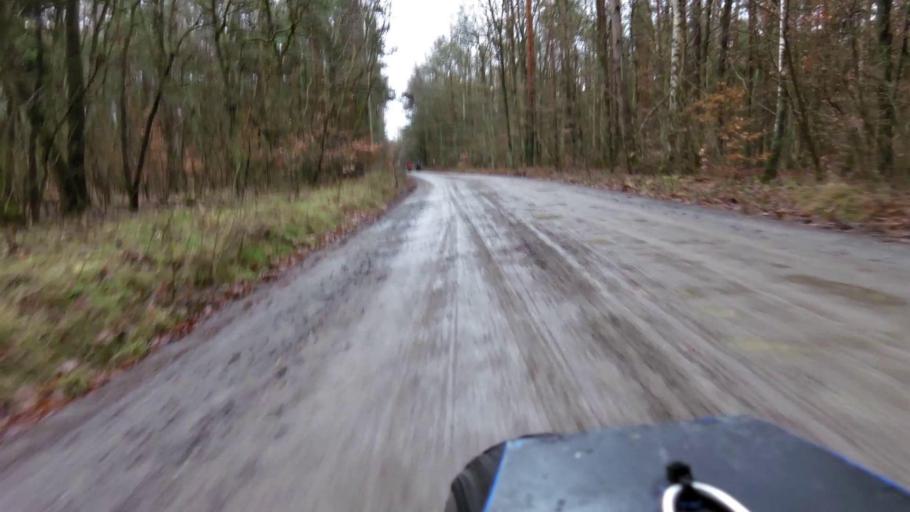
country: PL
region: Lubusz
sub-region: Powiat gorzowski
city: Witnica
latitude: 52.6940
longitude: 14.8486
